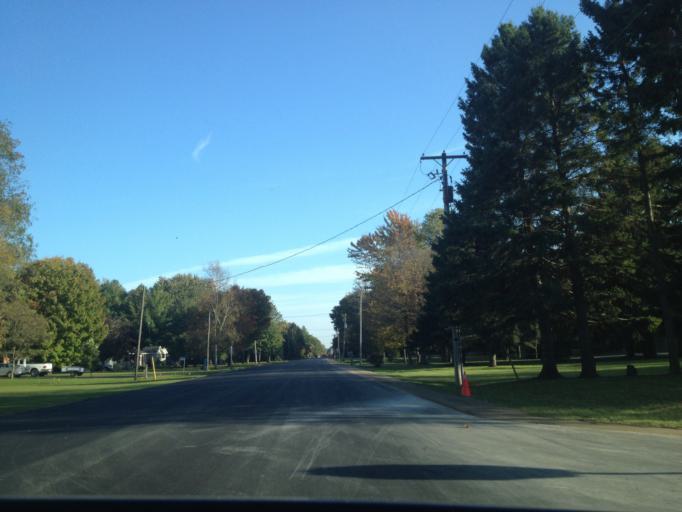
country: CA
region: Ontario
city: Delaware
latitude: 42.5785
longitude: -81.5757
